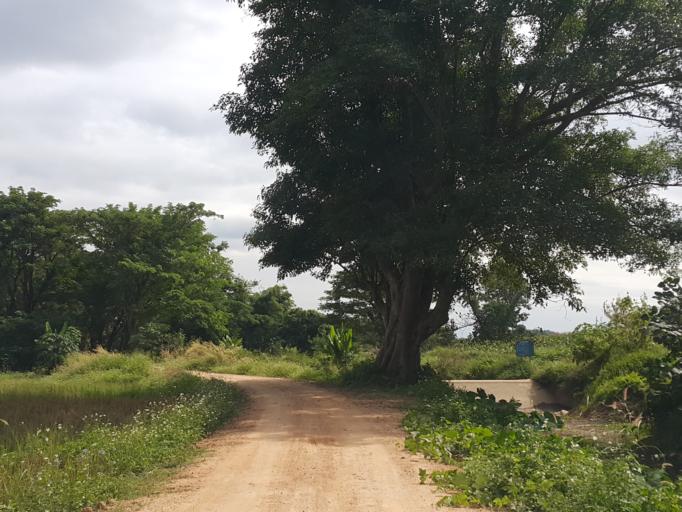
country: TH
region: Lampang
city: Hang Chat
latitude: 18.4876
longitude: 99.3997
